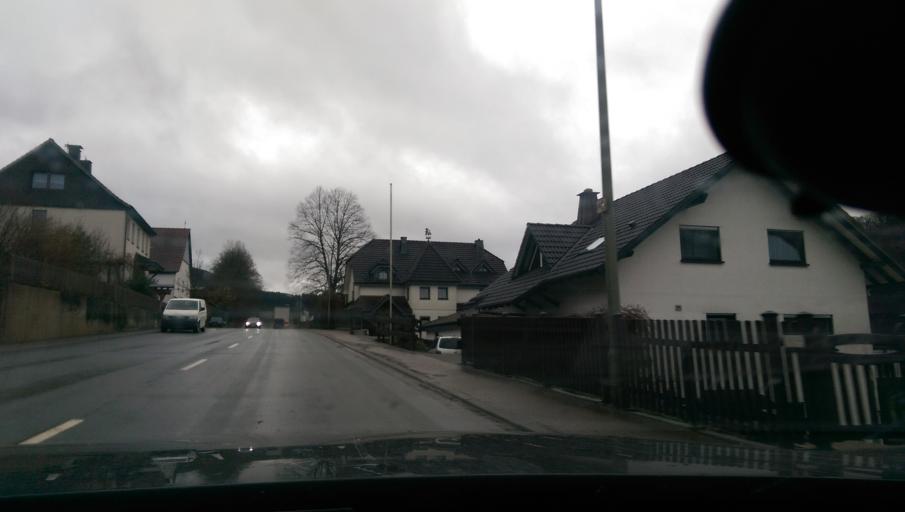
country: DE
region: North Rhine-Westphalia
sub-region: Regierungsbezirk Arnsberg
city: Finnentrop
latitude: 51.2146
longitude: 7.9614
